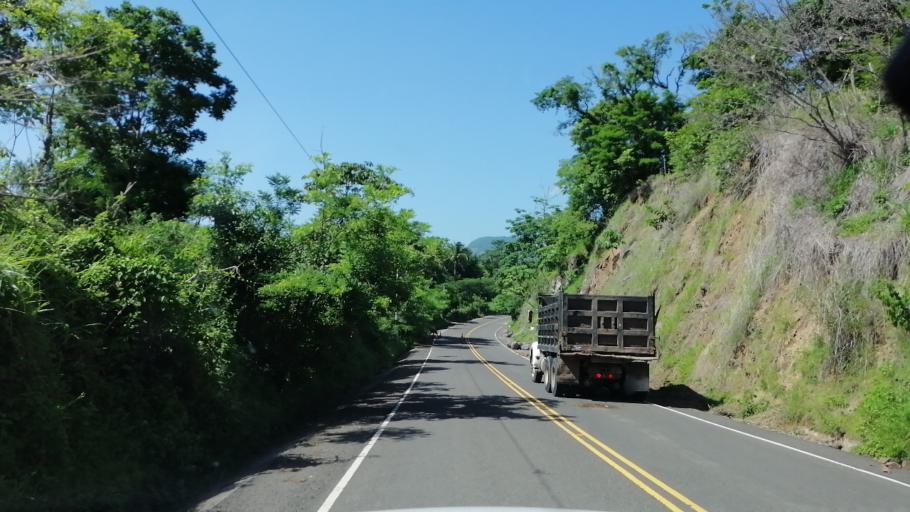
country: HN
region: Lempira
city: La Virtud
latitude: 13.9715
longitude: -88.7635
